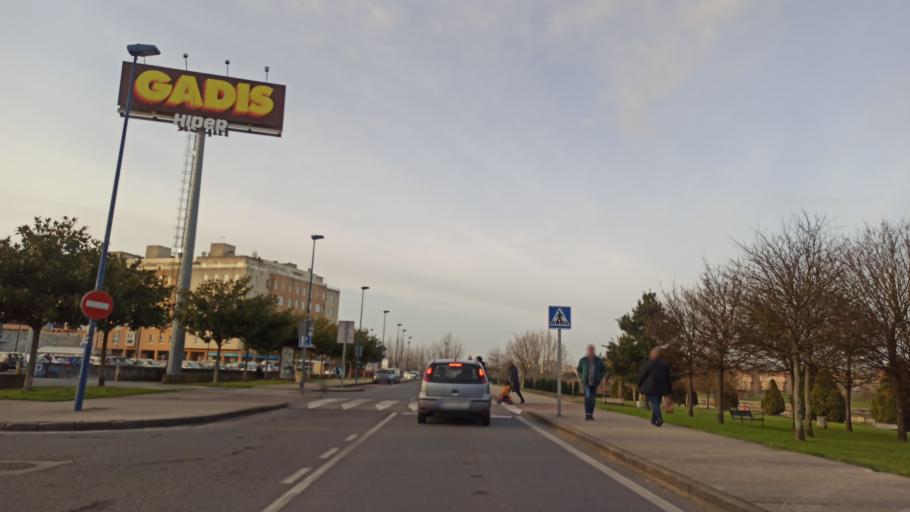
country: ES
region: Galicia
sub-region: Provincia da Coruna
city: Cambre
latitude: 43.3160
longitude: -8.3614
